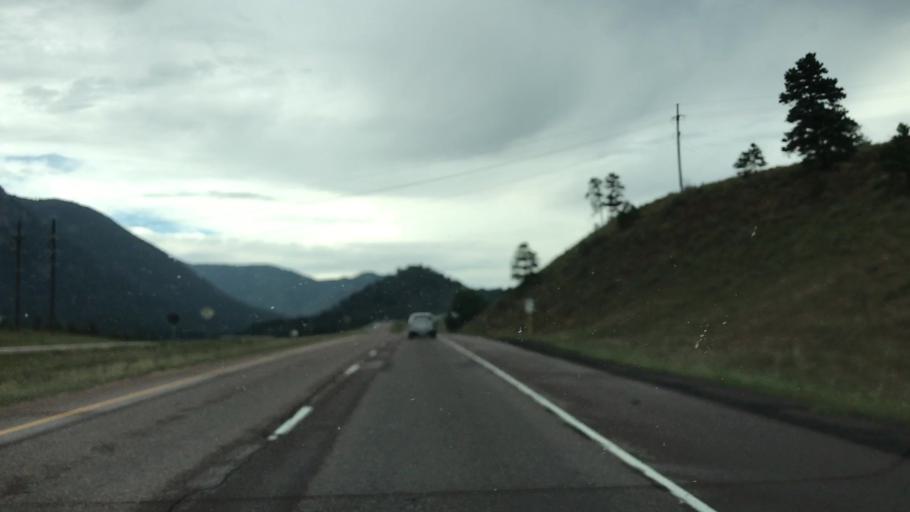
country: US
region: Colorado
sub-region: El Paso County
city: Cascade-Chipita Park
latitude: 38.9213
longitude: -104.9893
